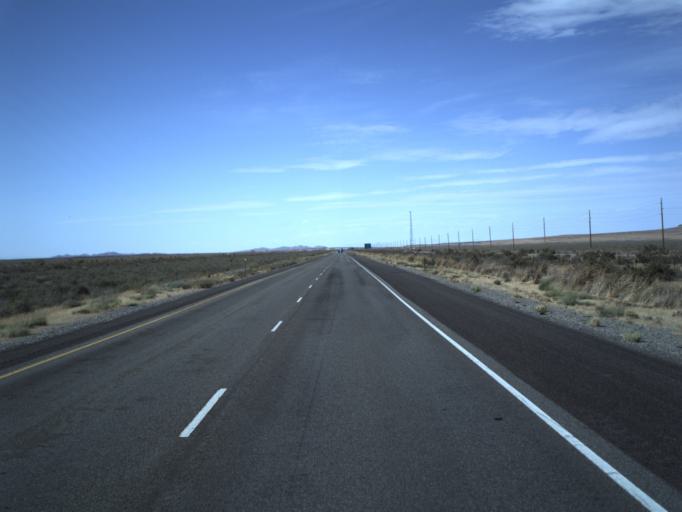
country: US
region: Utah
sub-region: Tooele County
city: Grantsville
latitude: 40.7414
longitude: -113.0813
